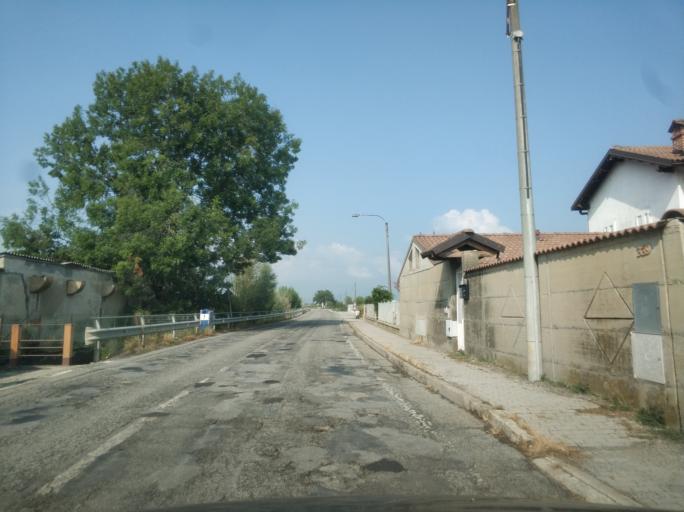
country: IT
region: Piedmont
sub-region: Provincia di Cuneo
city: Montanera
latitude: 44.5120
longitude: 7.6445
